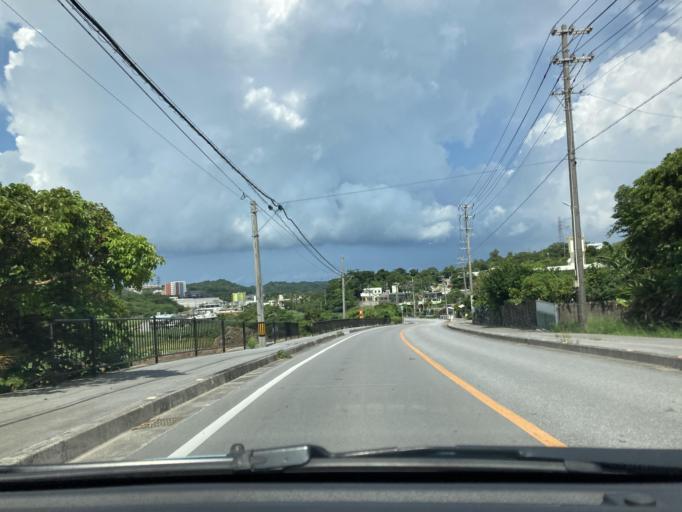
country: JP
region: Okinawa
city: Tomigusuku
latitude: 26.1588
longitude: 127.7783
